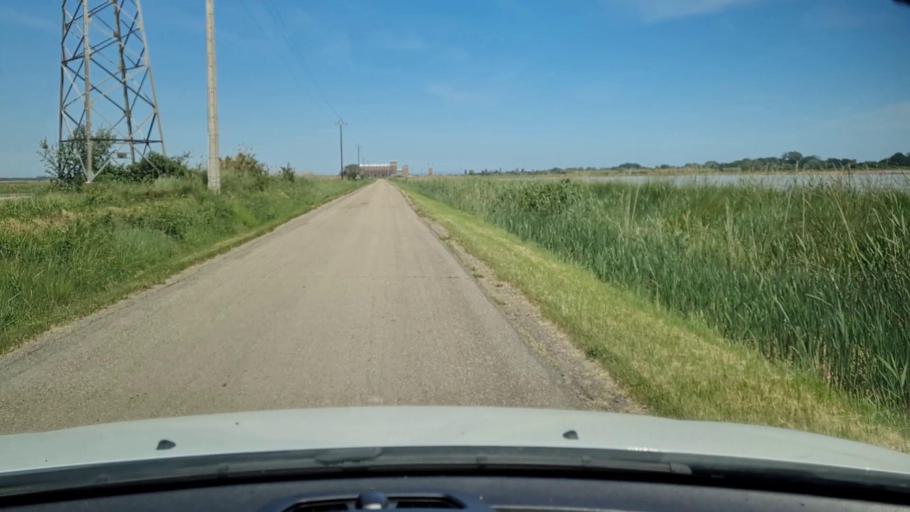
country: FR
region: Languedoc-Roussillon
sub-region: Departement du Gard
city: Saint-Gilles
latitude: 43.5796
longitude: 4.3997
